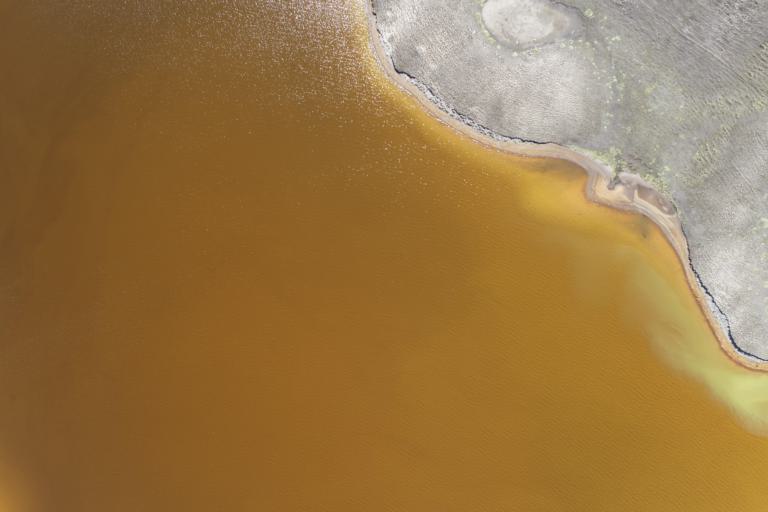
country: BO
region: La Paz
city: La Paz
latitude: -16.3459
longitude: -68.1622
